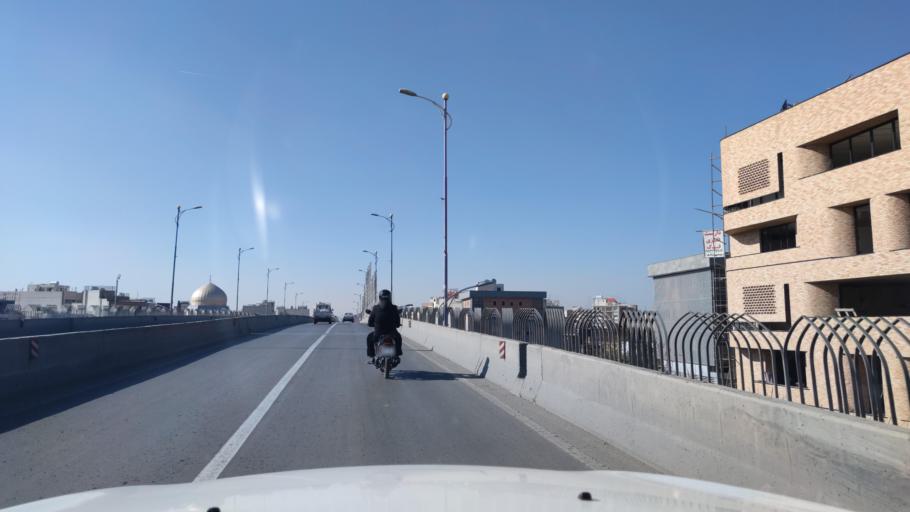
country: IR
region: Isfahan
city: Isfahan
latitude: 32.6791
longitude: 51.6733
